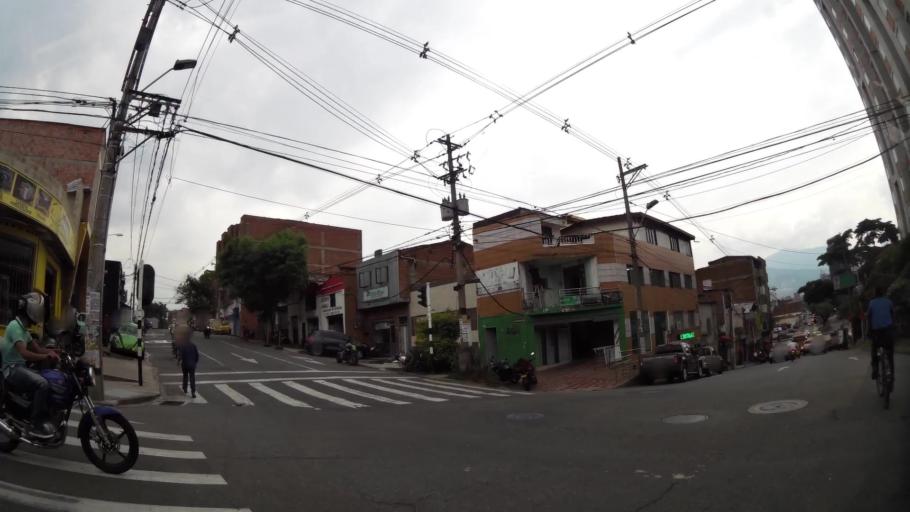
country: CO
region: Antioquia
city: Medellin
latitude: 6.2407
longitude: -75.5688
